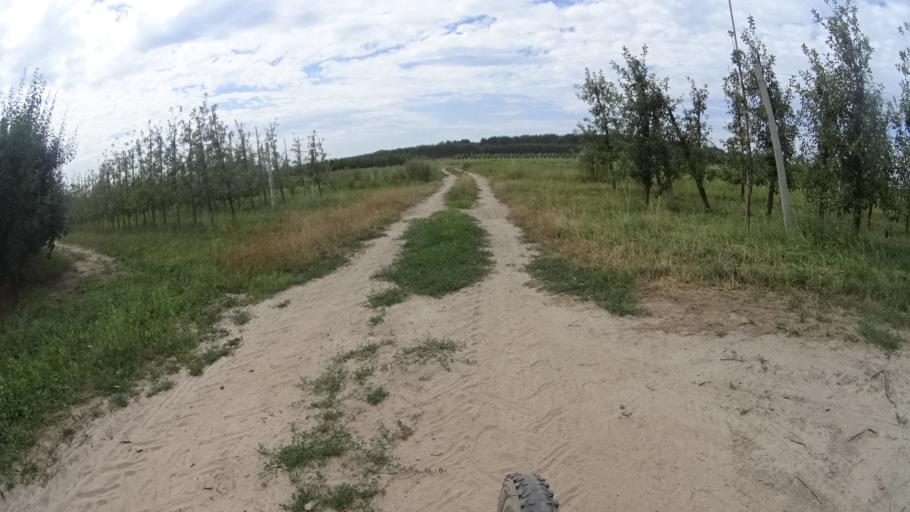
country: PL
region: Masovian Voivodeship
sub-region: Powiat bialobrzeski
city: Wysmierzyce
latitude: 51.6547
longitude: 20.7940
